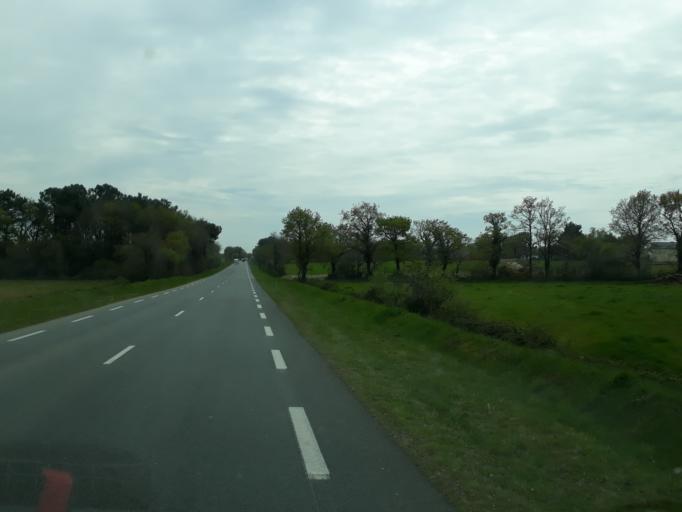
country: FR
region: Brittany
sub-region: Departement du Morbihan
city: Ferel
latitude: 47.5240
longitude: -2.3783
